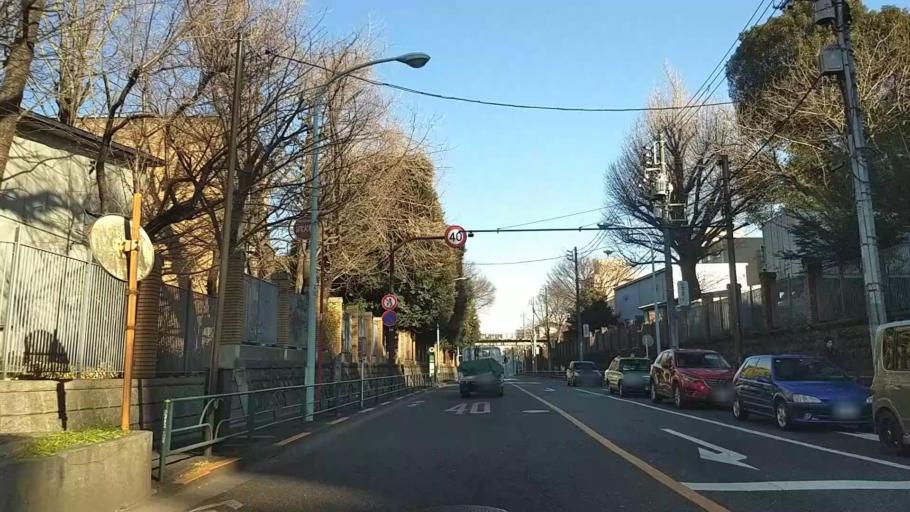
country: JP
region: Tokyo
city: Tokyo
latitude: 35.7156
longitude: 139.7589
